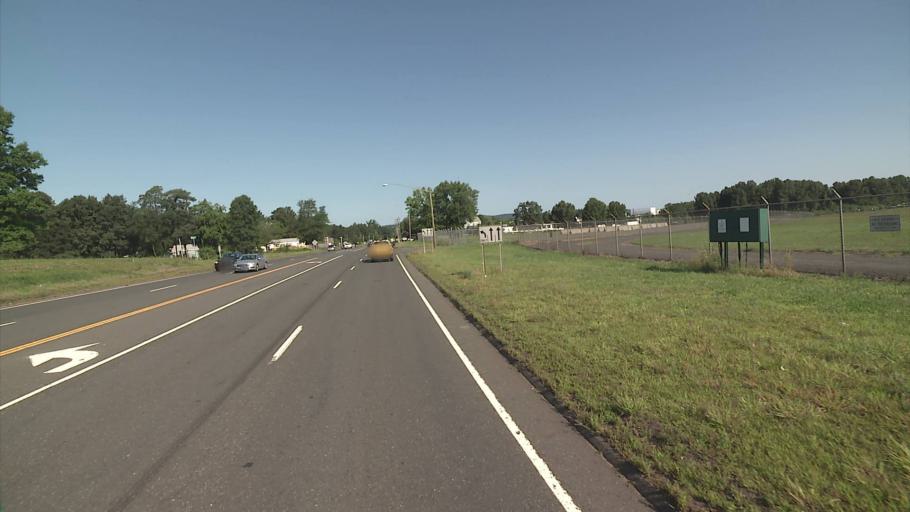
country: US
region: Connecticut
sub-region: Hartford County
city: Tariffville
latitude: 41.9263
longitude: -72.7053
